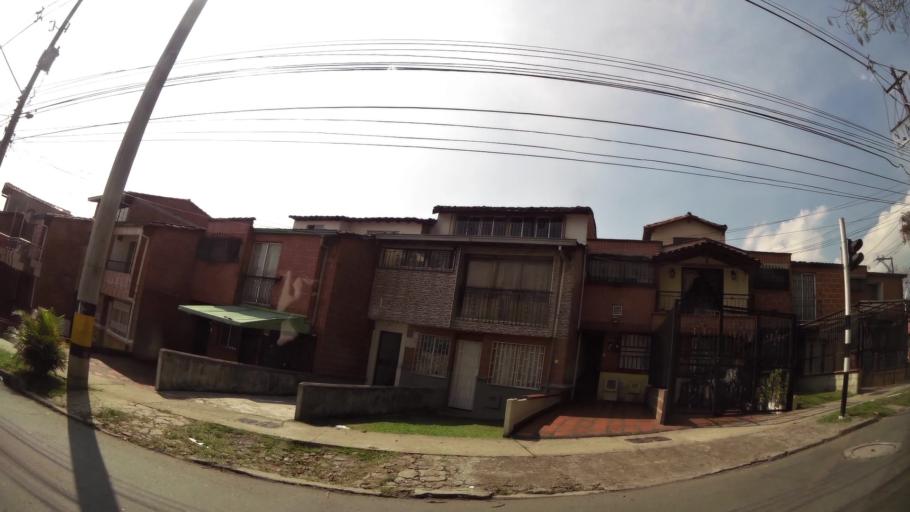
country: CO
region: Antioquia
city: La Estrella
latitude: 6.1687
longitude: -75.6403
